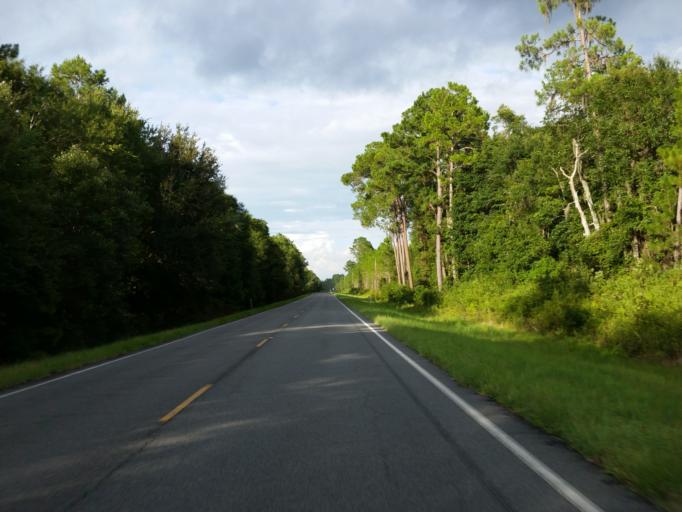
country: US
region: Florida
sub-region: Hamilton County
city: Jasper
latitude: 30.6333
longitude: -82.5929
